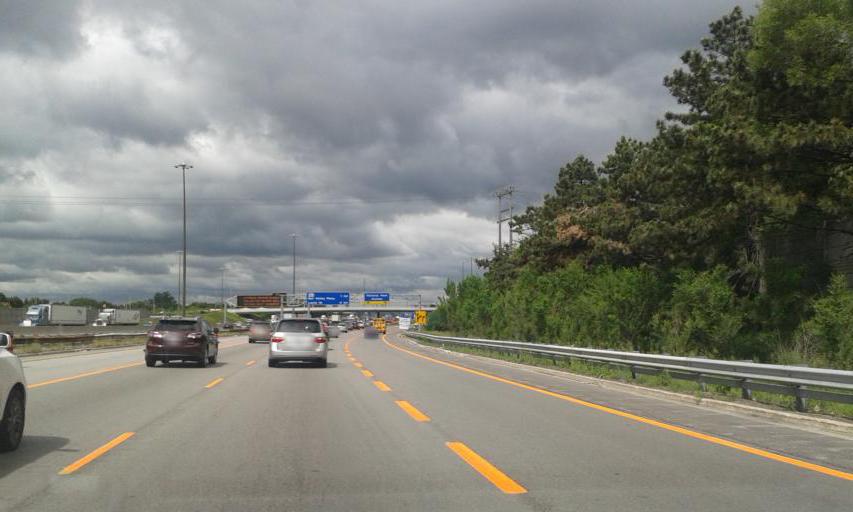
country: CA
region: Ontario
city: Scarborough
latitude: 43.7688
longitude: -79.3131
